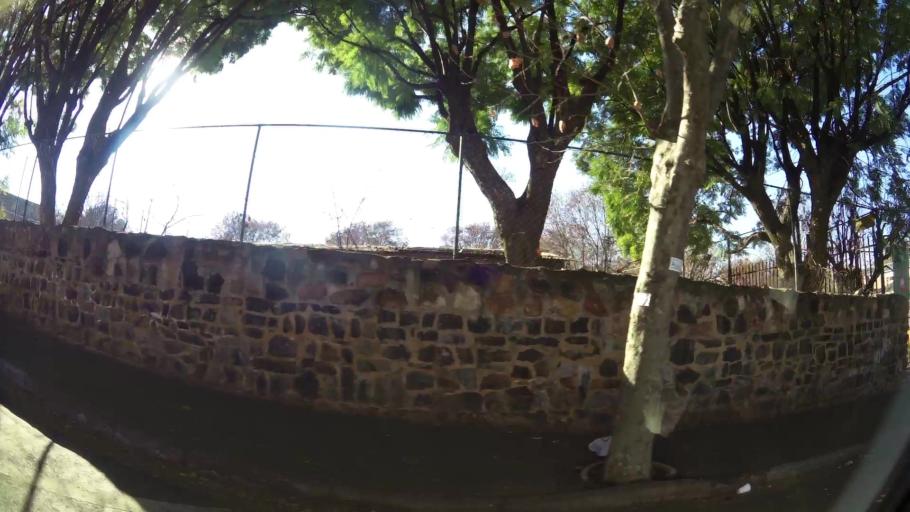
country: ZA
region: Gauteng
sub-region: City of Johannesburg Metropolitan Municipality
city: Johannesburg
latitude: -26.2044
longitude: 28.0745
